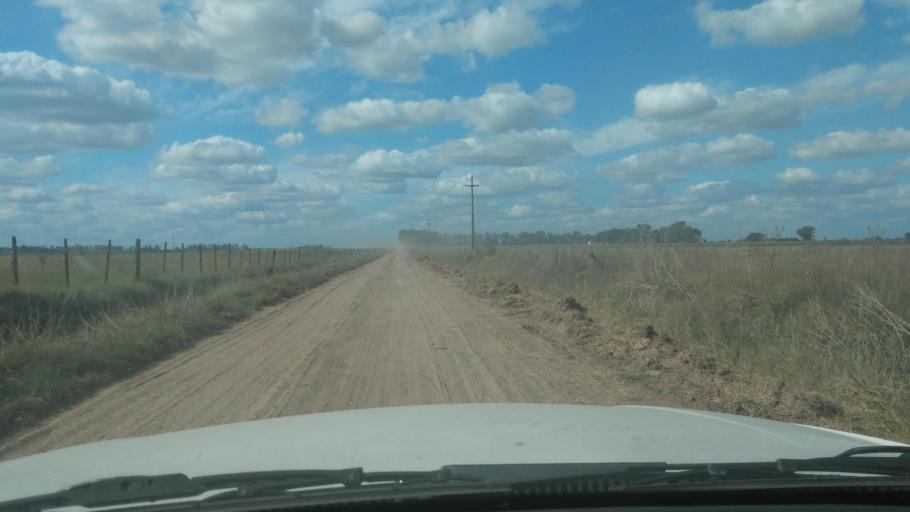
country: AR
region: Buenos Aires
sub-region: Partido de Navarro
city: Navarro
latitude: -35.0368
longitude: -59.5082
